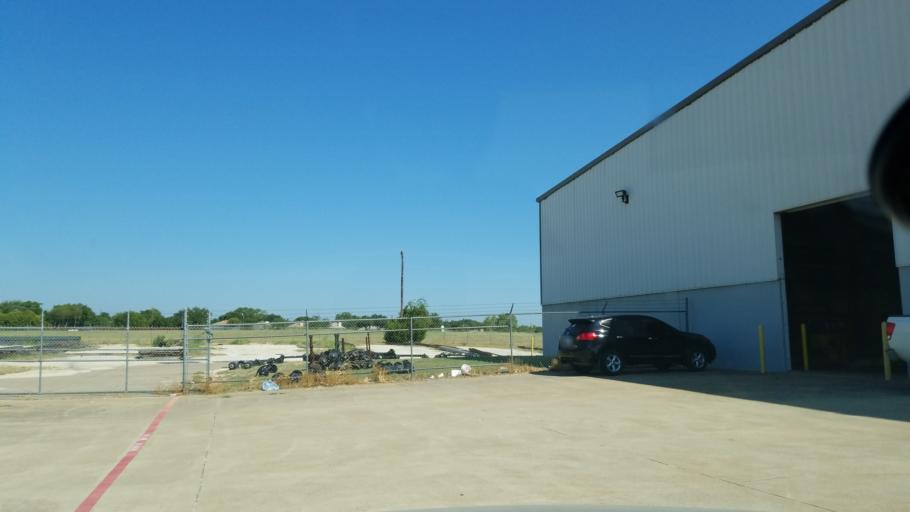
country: US
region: Texas
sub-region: Tarrant County
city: Mansfield
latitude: 32.5504
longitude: -97.1300
